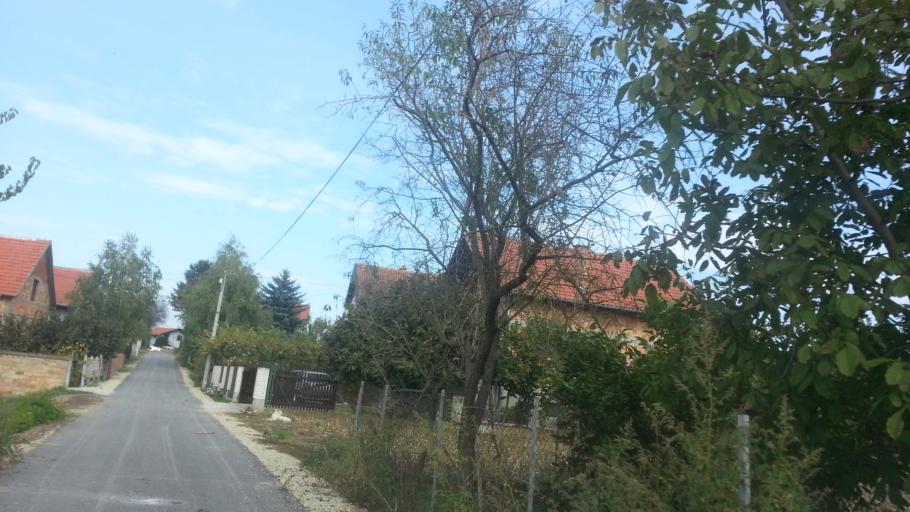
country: RS
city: Surduk
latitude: 45.0651
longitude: 20.3322
